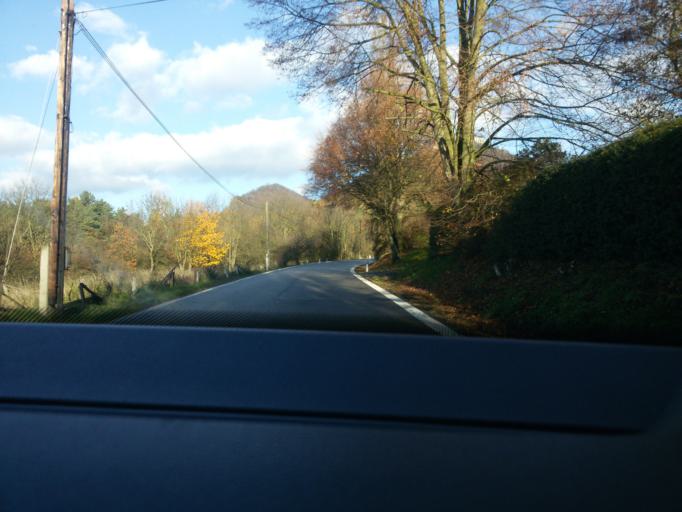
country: CZ
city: Doksy
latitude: 50.5295
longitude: 14.7229
